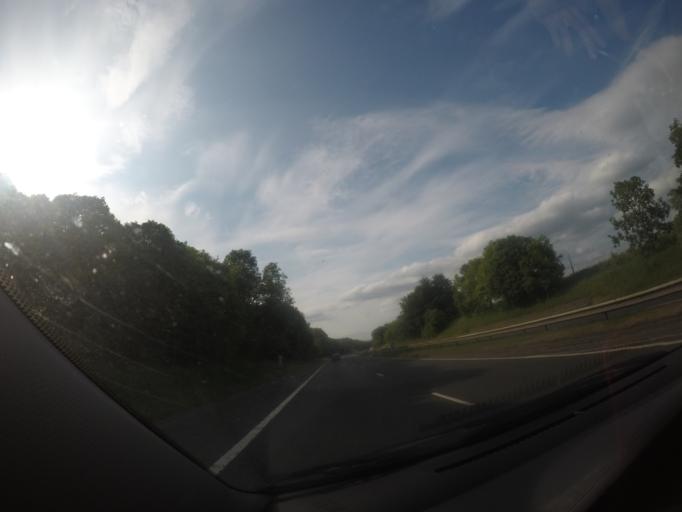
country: GB
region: Scotland
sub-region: South Lanarkshire
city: Larkhall
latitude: 55.7457
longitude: -3.9614
